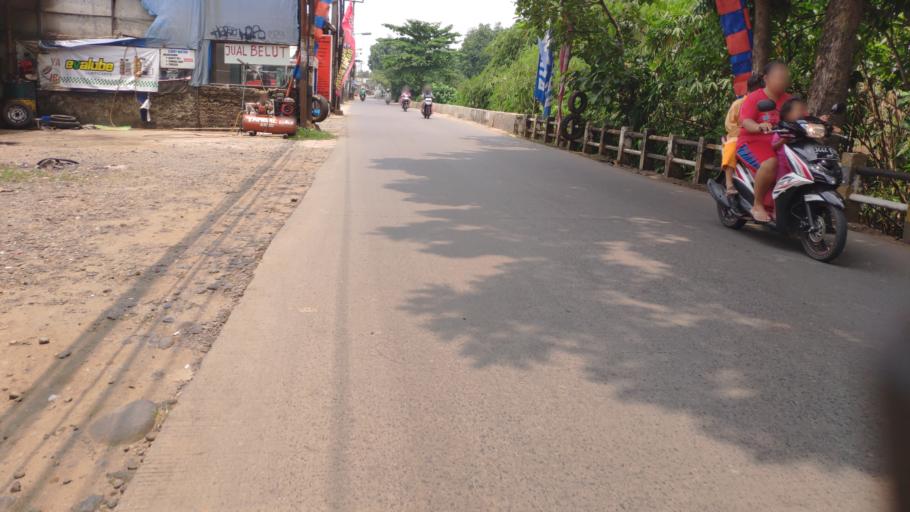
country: ID
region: West Java
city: Sawangan
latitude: -6.3783
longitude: 106.7900
